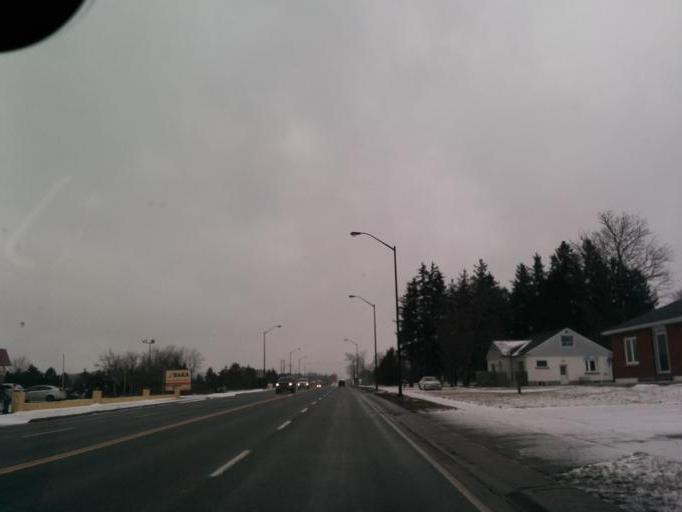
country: CA
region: Ontario
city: Orangeville
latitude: 43.8619
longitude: -79.9979
